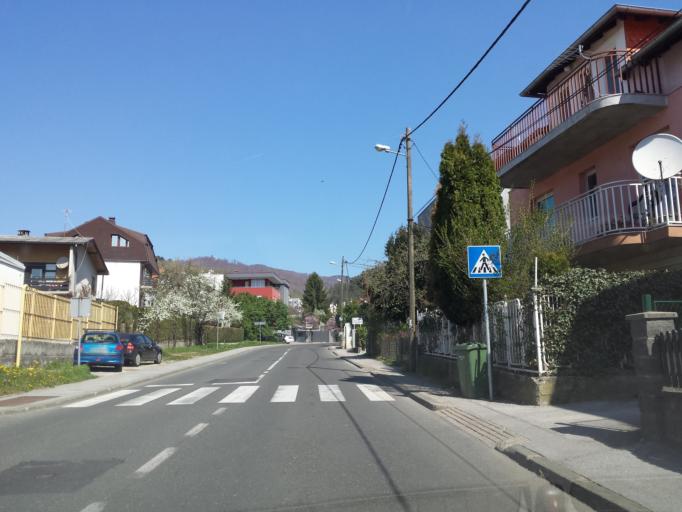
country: HR
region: Grad Zagreb
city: Zagreb
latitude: 45.8550
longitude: 15.9746
